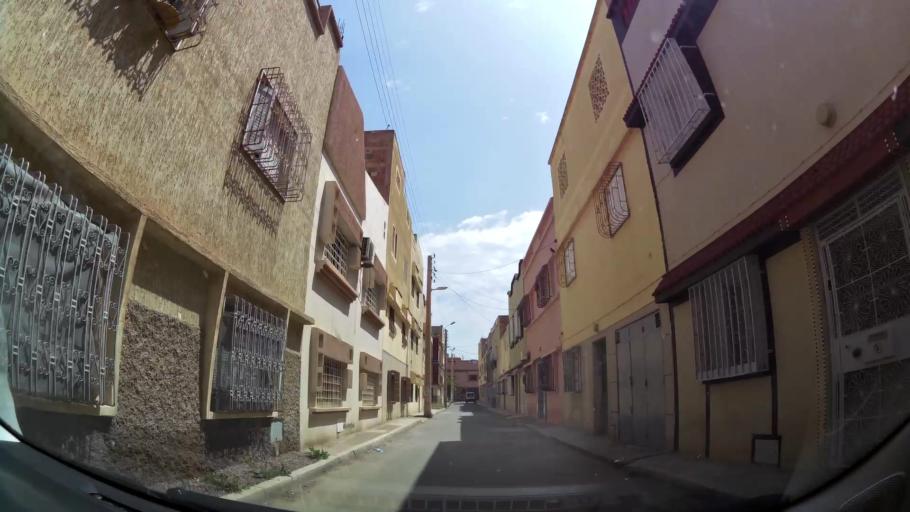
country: MA
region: Oriental
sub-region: Oujda-Angad
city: Oujda
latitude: 34.6827
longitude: -1.8847
